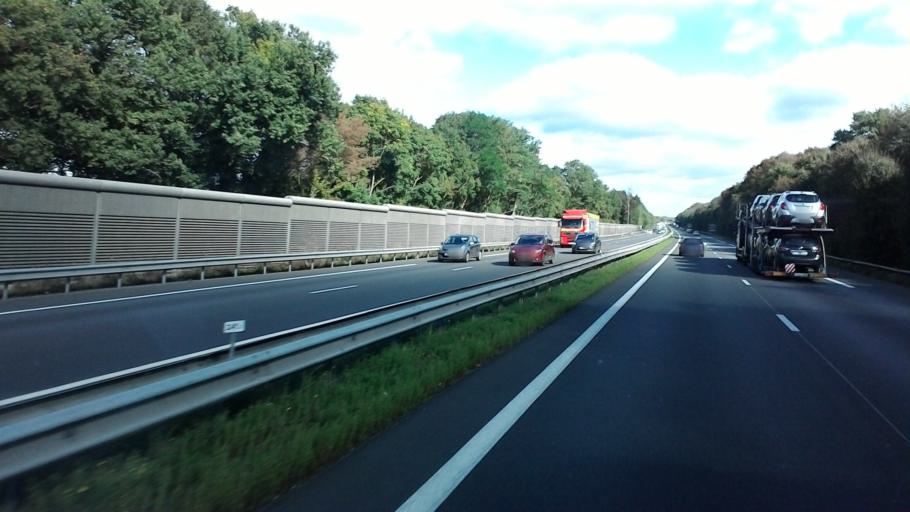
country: FR
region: Lorraine
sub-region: Departement de Meurthe-et-Moselle
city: Velaine-en-Haye
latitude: 48.6890
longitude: 6.0191
